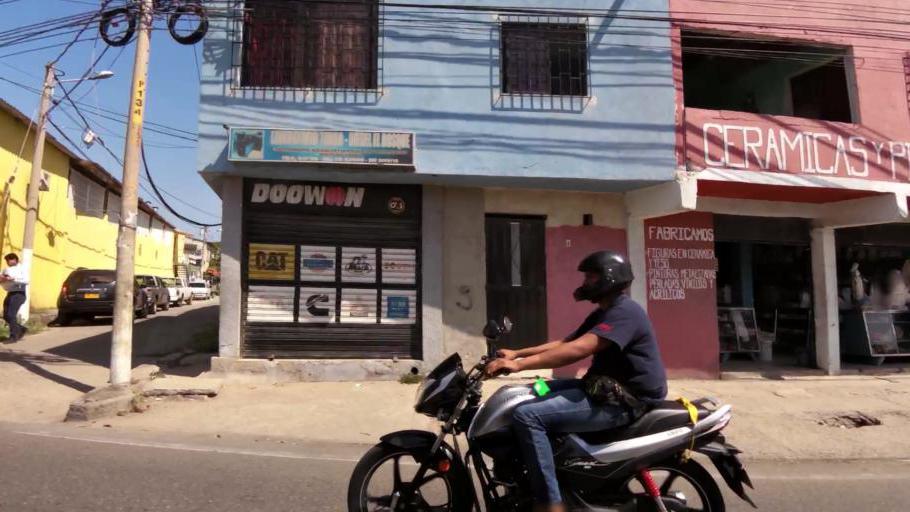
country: CO
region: Bolivar
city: Cartagena
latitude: 10.3891
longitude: -75.5148
